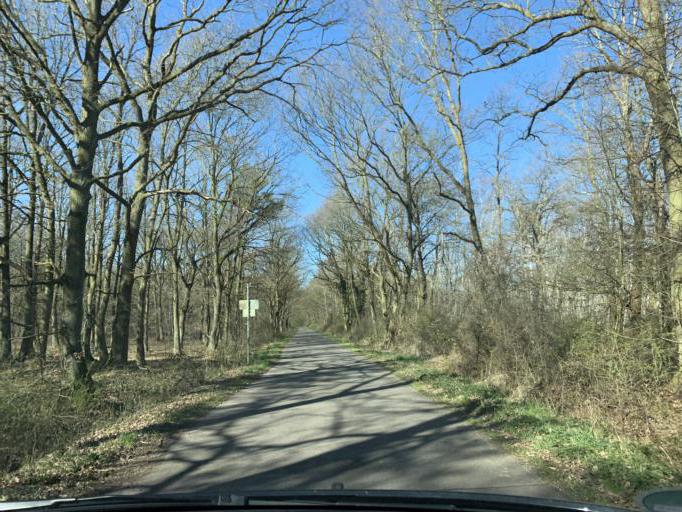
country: DE
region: North Rhine-Westphalia
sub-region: Regierungsbezirk Koln
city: Nideggen
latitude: 50.7078
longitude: 6.5363
